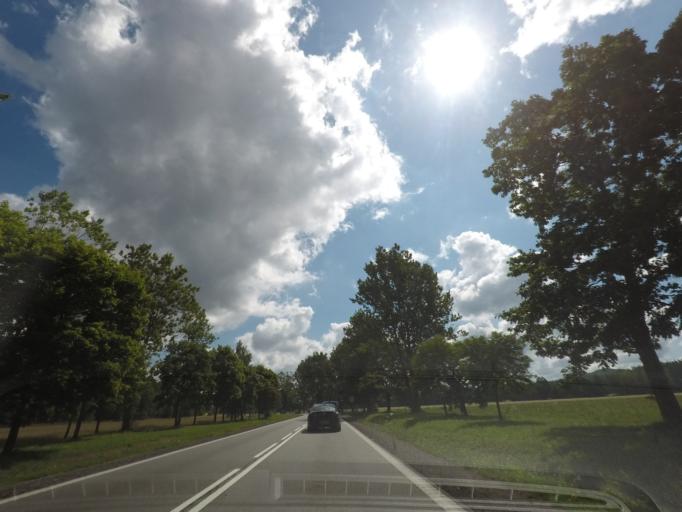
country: PL
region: Pomeranian Voivodeship
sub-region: Powiat wejherowski
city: Leczyce
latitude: 54.5698
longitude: 17.9591
